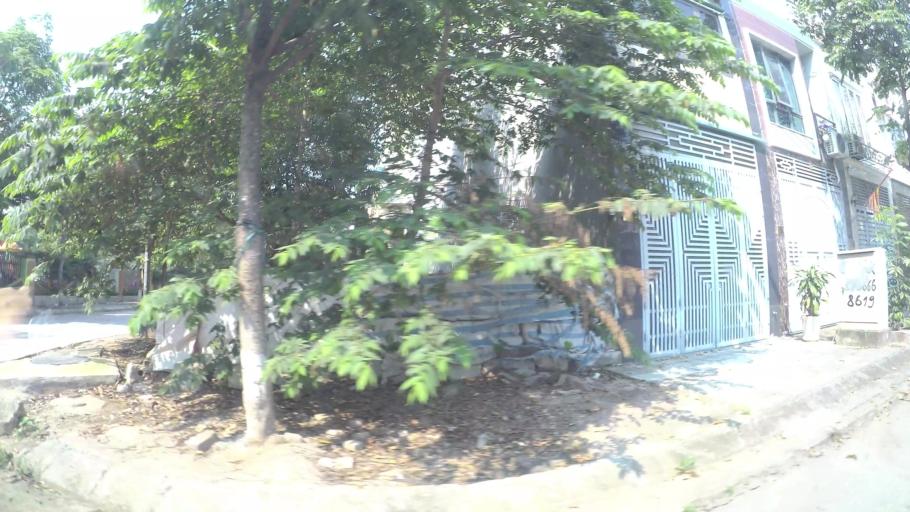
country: VN
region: Ha Noi
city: Ha Dong
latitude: 20.9557
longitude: 105.8053
